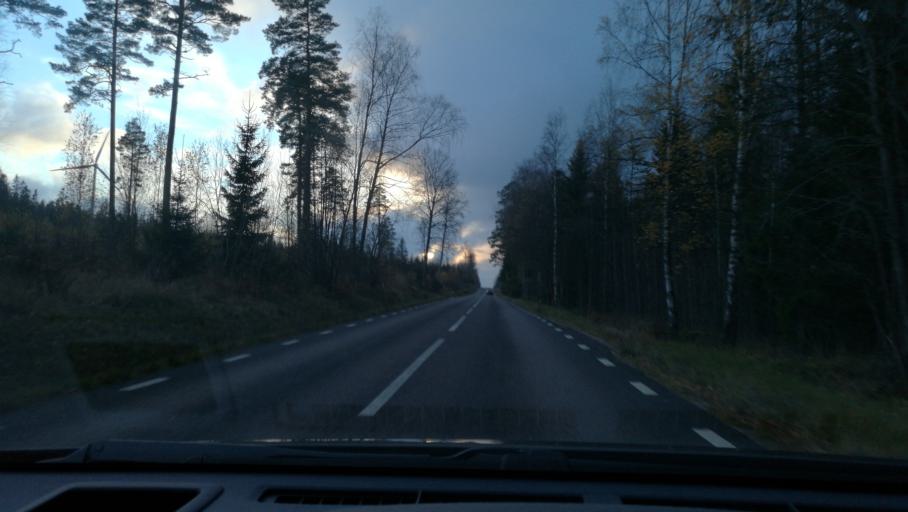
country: SE
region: Soedermanland
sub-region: Vingakers Kommun
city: Vingaker
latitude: 59.1428
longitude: 15.8666
